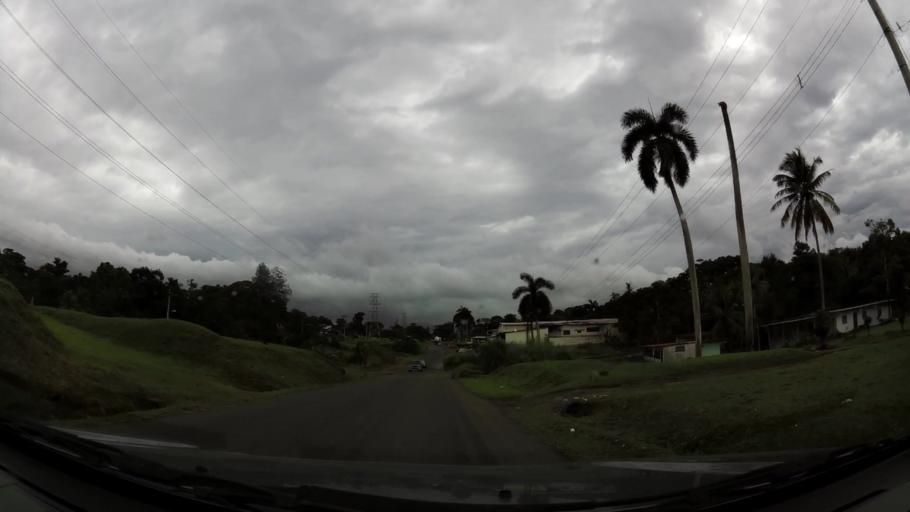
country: PA
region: Panama
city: Chilibre
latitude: 9.1475
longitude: -79.6177
